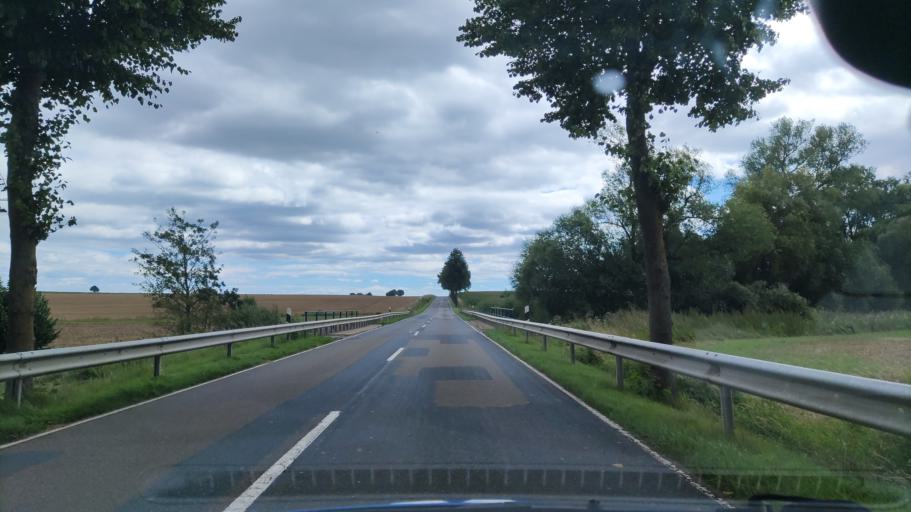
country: DE
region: Lower Saxony
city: Wangelnstedt
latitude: 51.8417
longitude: 9.7296
